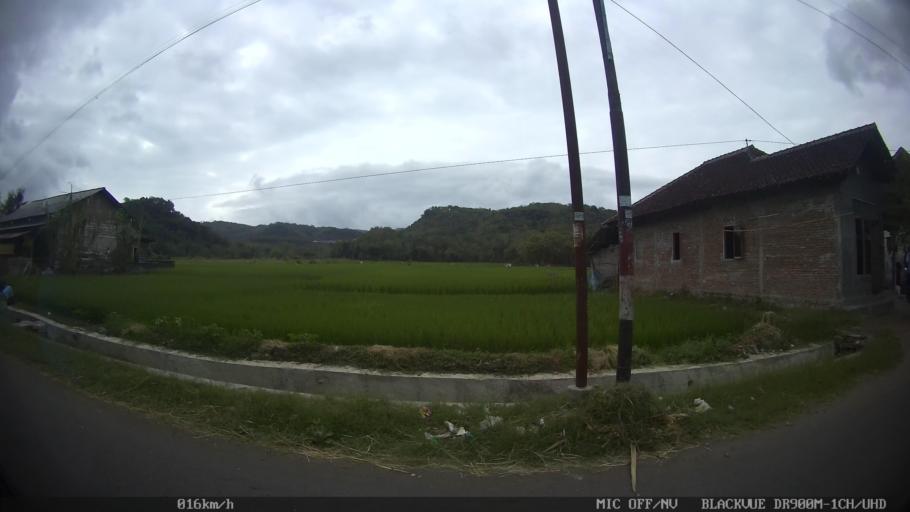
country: ID
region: Daerah Istimewa Yogyakarta
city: Sewon
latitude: -7.8700
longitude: 110.4185
